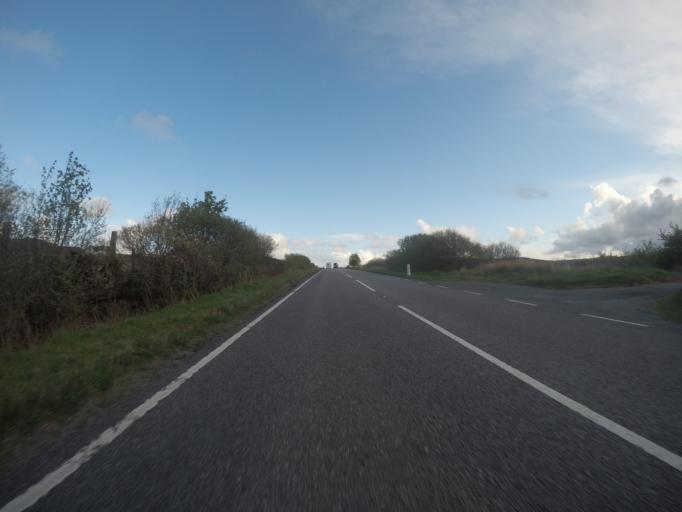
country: GB
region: Scotland
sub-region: Highland
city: Portree
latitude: 57.4775
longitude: -6.3000
